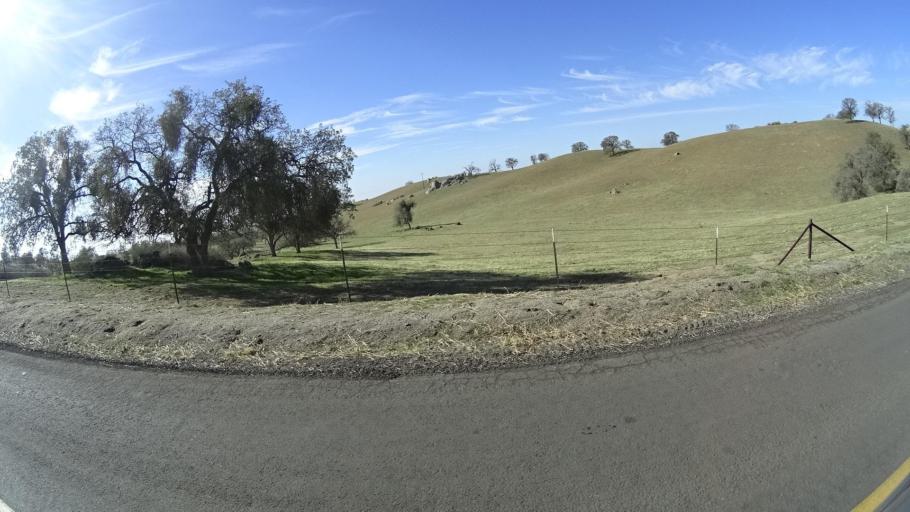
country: US
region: California
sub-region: Kern County
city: Oildale
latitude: 35.6456
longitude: -118.8401
